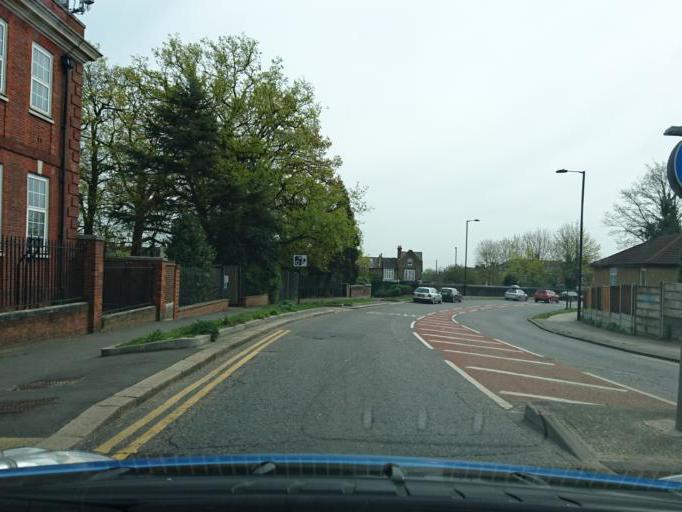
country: GB
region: England
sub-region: Greater London
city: Wood Green
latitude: 51.6256
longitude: -0.1069
